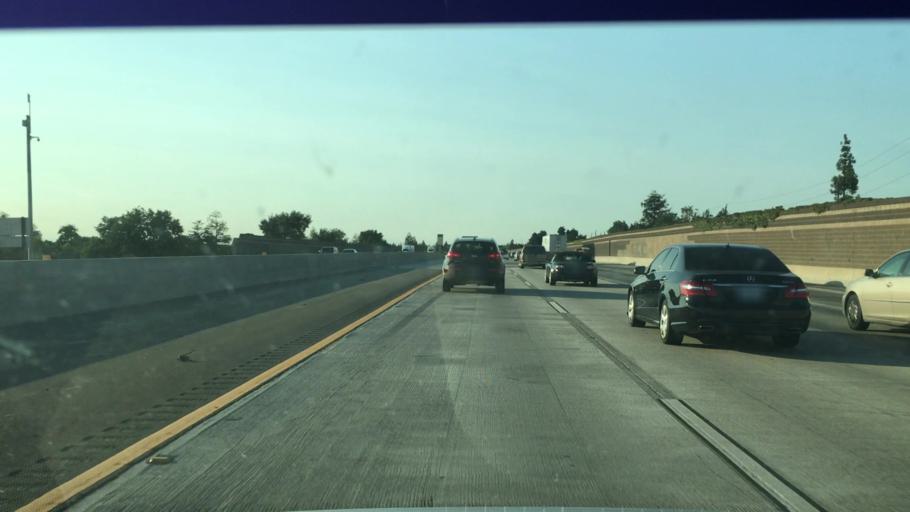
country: US
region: California
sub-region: San Joaquin County
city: Country Club
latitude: 37.9639
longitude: -121.3351
